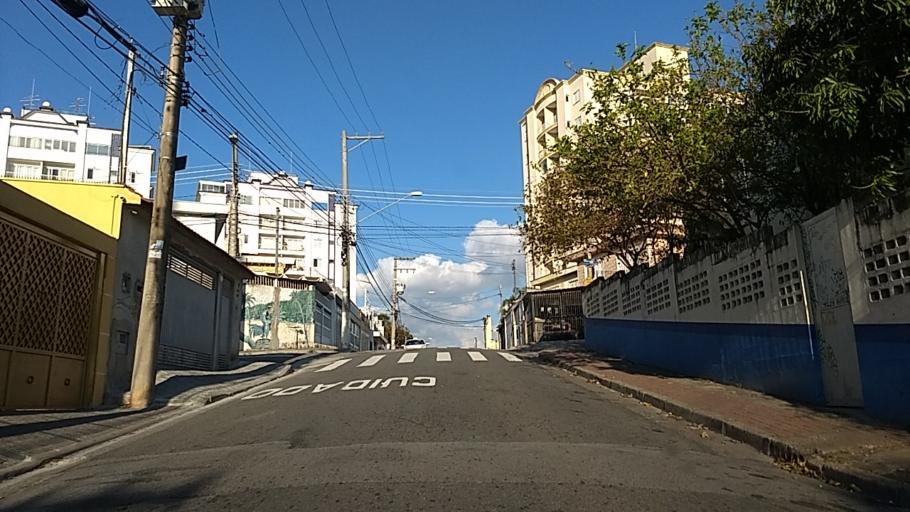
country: BR
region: Sao Paulo
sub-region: Sao Paulo
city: Sao Paulo
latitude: -23.4929
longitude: -46.6009
